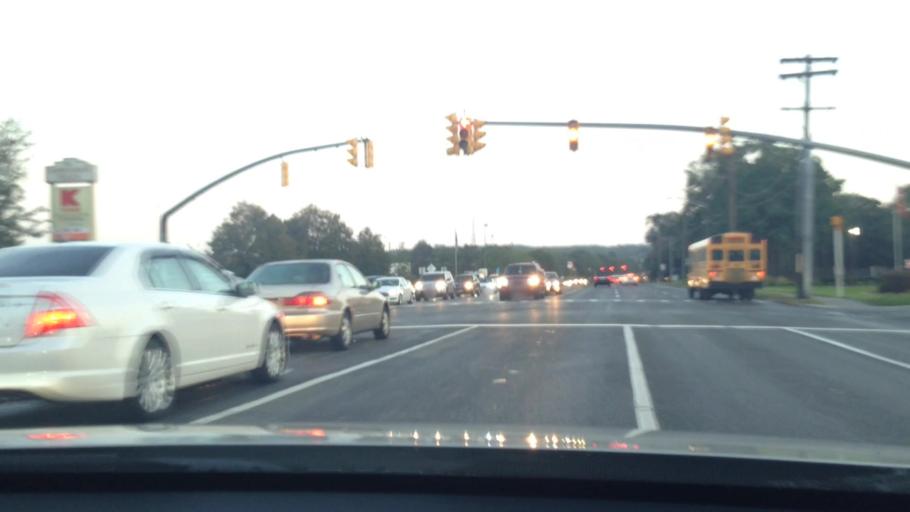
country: US
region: New York
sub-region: Suffolk County
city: Farmingville
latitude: 40.8266
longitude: -73.0206
